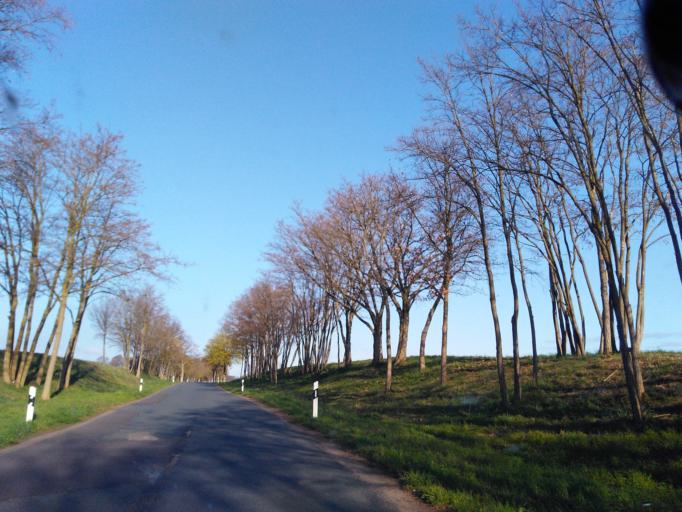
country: DE
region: Brandenburg
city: Protzel
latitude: 52.6588
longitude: 14.0490
